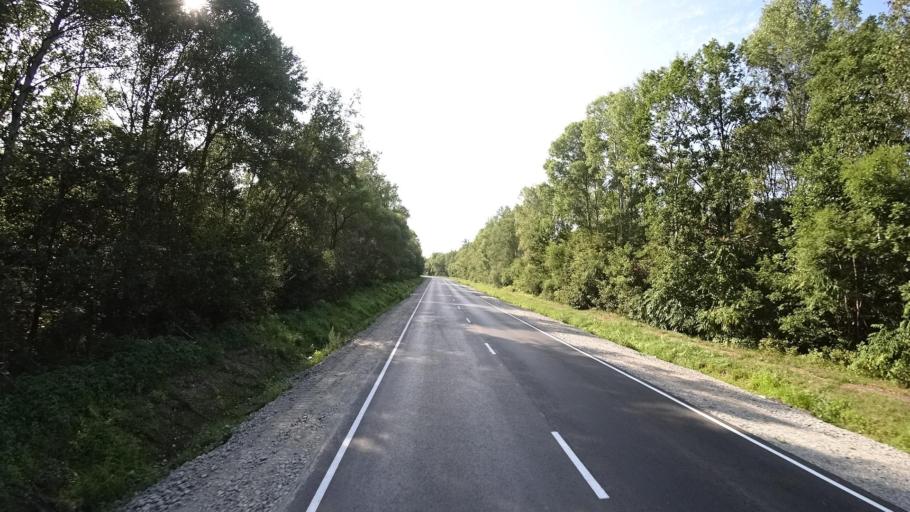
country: RU
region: Khabarovsk Krai
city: Khor
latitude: 47.9760
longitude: 135.0778
